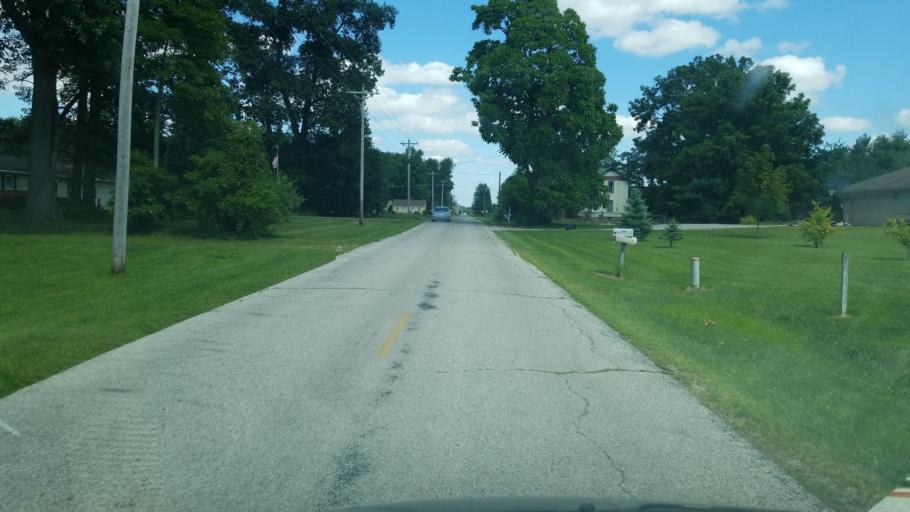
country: US
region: Ohio
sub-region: Henry County
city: Liberty Center
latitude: 41.4991
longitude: -83.9413
